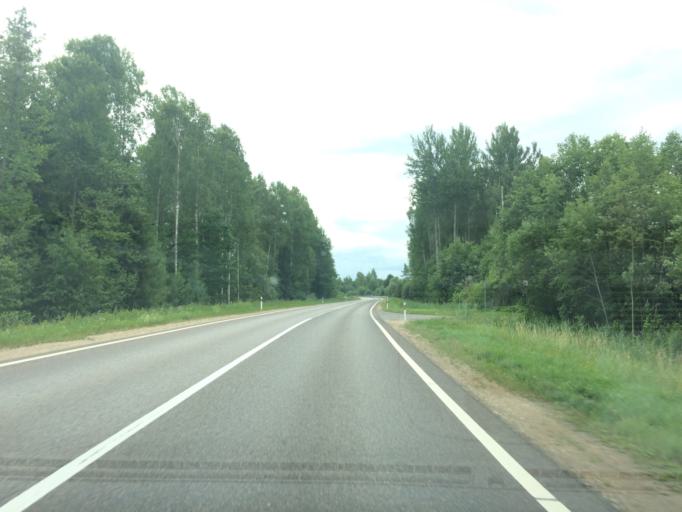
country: LV
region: Livani
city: Livani
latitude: 56.5344
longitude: 26.1387
